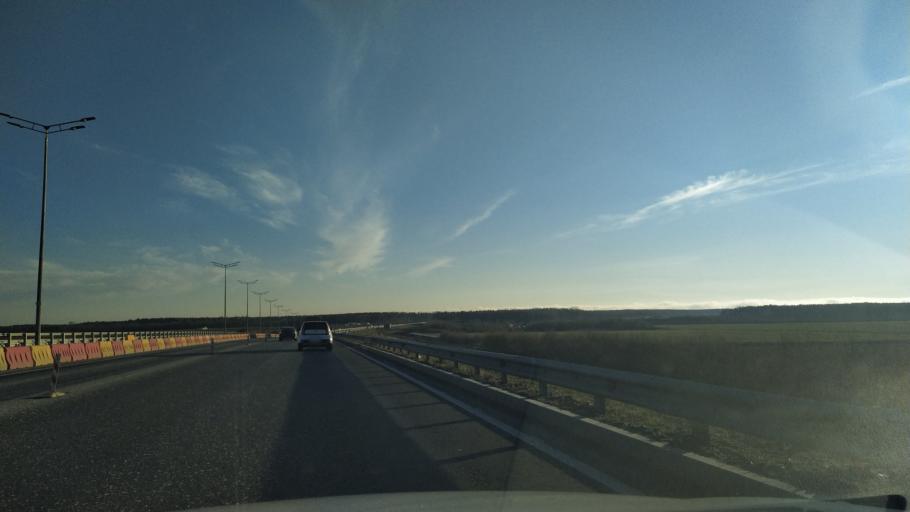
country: RU
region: St.-Petersburg
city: Pargolovo
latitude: 60.0910
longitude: 30.2425
